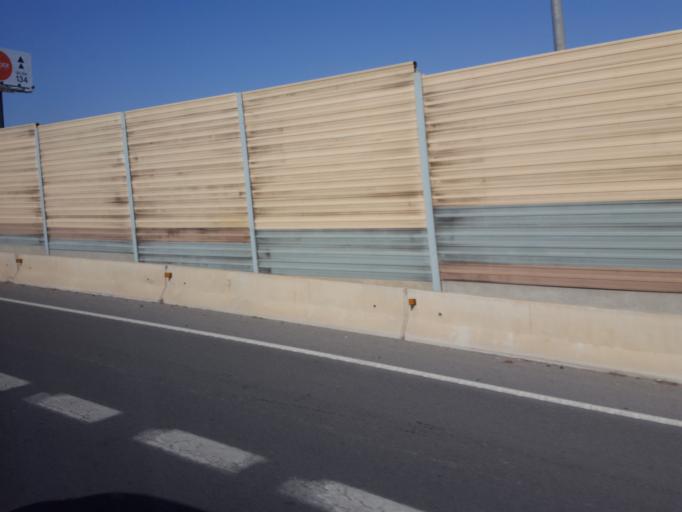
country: ES
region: Murcia
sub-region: Murcia
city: Murcia
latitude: 38.0007
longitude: -1.1563
